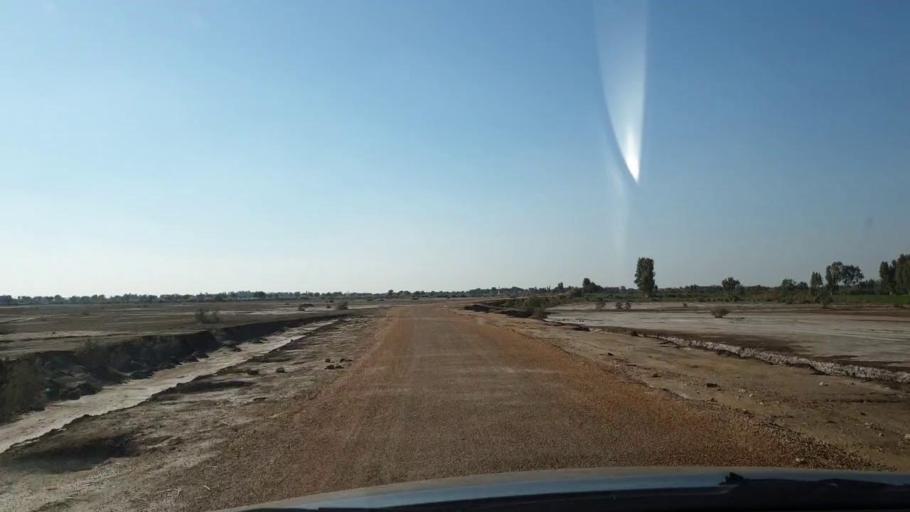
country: PK
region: Sindh
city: Jhol
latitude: 25.8920
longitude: 69.0280
